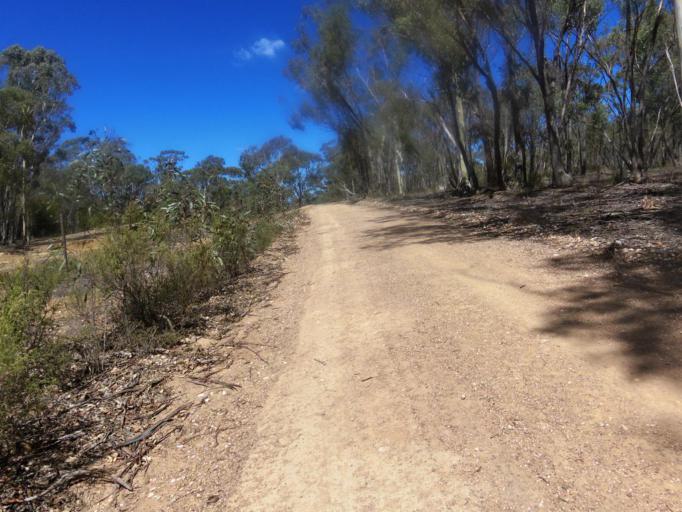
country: AU
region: Victoria
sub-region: Mount Alexander
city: Castlemaine
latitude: -37.0545
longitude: 144.1881
